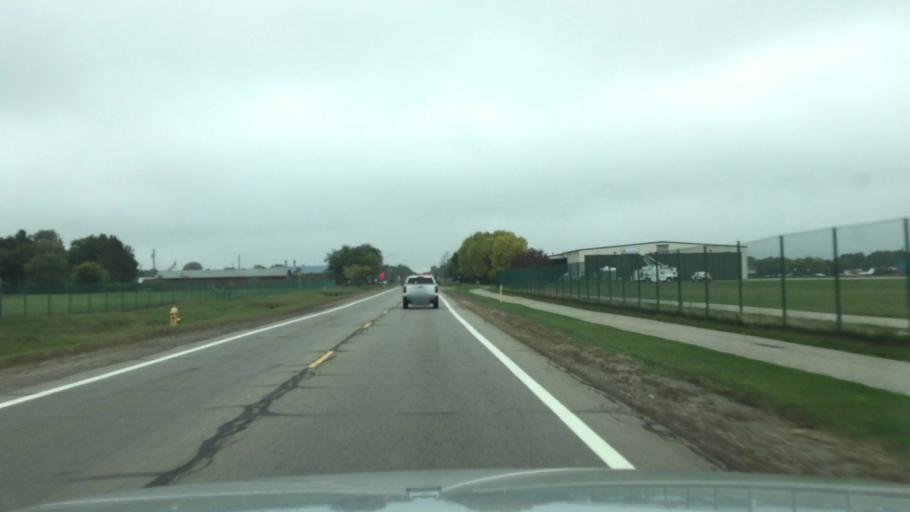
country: US
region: Michigan
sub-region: Oakland County
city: Waterford
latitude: 42.6653
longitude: -83.4062
